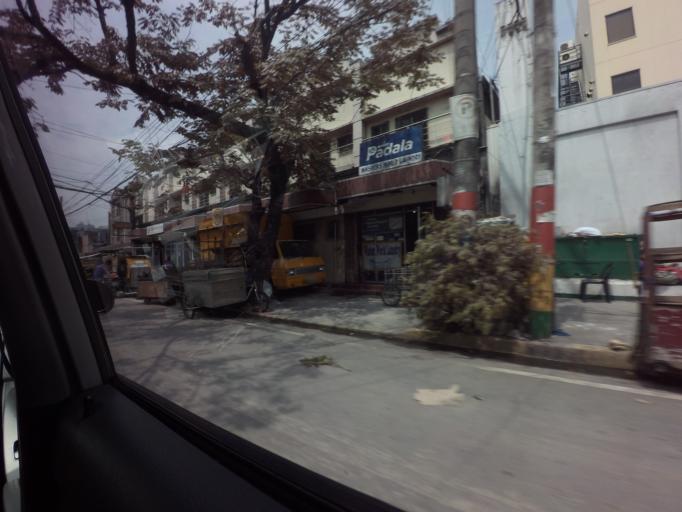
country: PH
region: Metro Manila
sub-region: City of Manila
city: Quiapo
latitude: 14.5764
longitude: 120.9908
